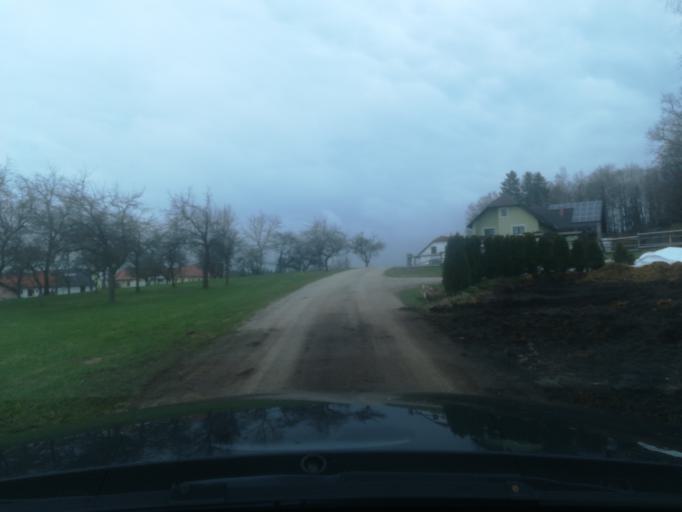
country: AT
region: Upper Austria
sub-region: Politischer Bezirk Rohrbach
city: Kleinzell im Muehlkreis
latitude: 48.3705
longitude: 13.9181
